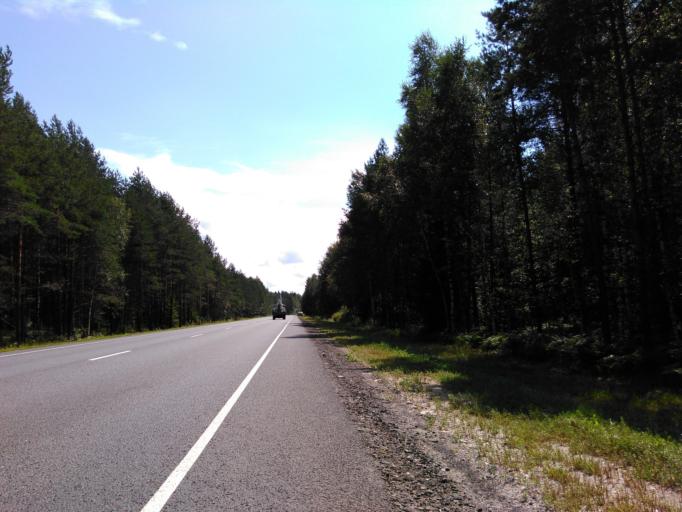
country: RU
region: Moskovskaya
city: Elektrogorsk
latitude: 56.0279
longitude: 38.7555
